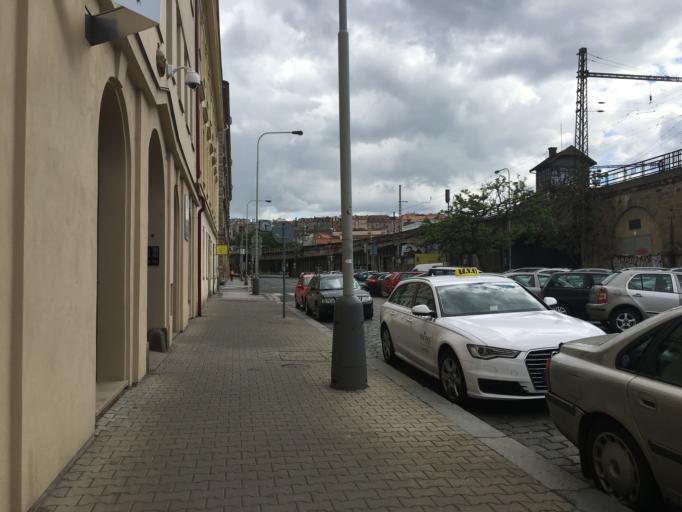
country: CZ
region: Praha
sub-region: Praha 8
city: Karlin
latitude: 50.0912
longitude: 14.4427
